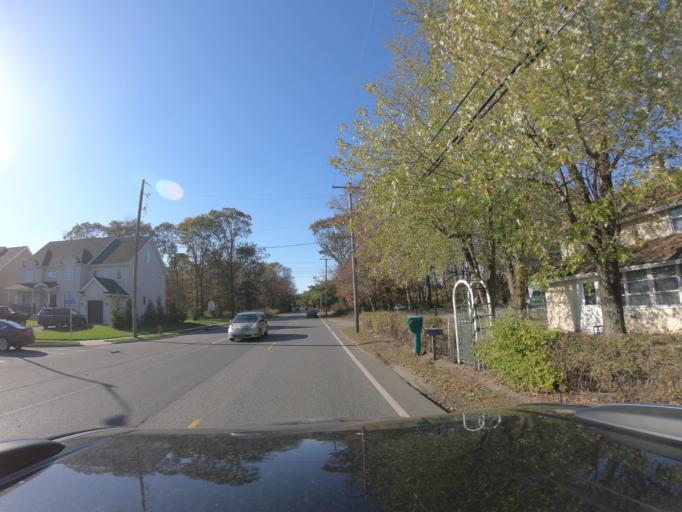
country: US
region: New Jersey
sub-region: Monmouth County
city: Ramtown
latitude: 40.1043
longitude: -74.1786
